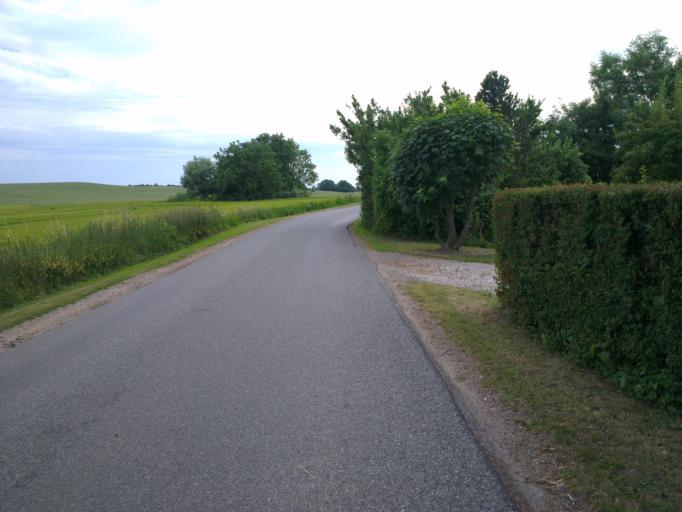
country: DK
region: Capital Region
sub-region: Frederikssund Kommune
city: Skibby
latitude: 55.7520
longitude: 12.0103
